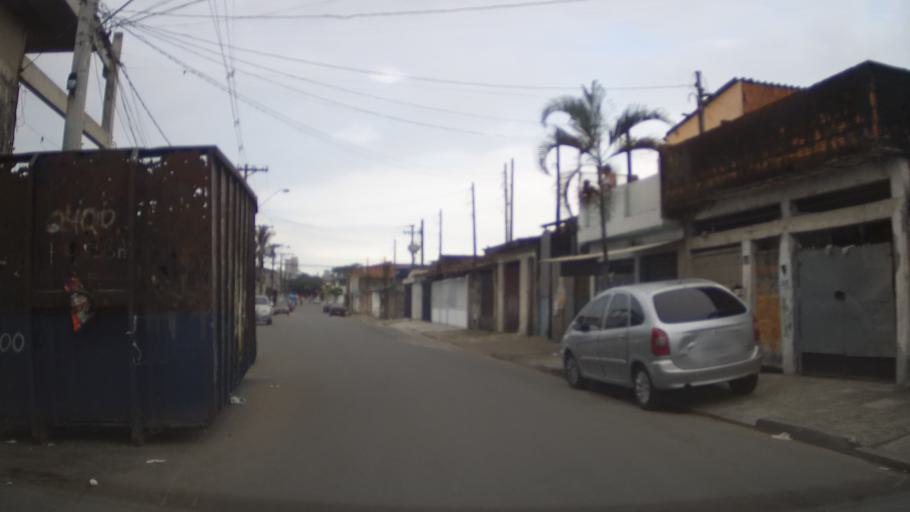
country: BR
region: Sao Paulo
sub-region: Praia Grande
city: Praia Grande
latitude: -24.0031
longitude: -46.4438
